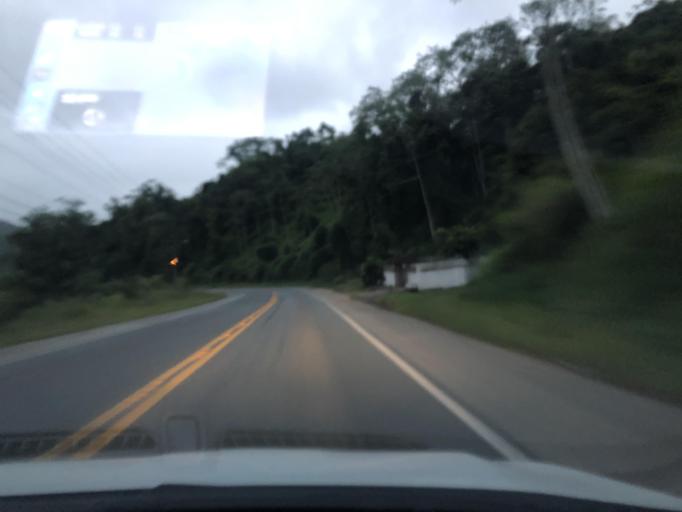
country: BR
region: Santa Catarina
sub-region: Jaragua Do Sul
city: Jaragua do Sul
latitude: -26.6516
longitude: -49.0237
